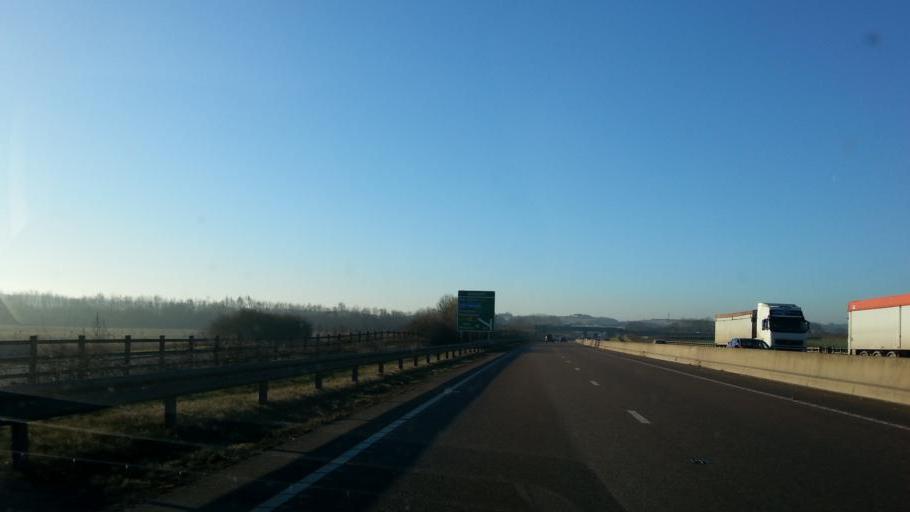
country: GB
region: England
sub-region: Nottinghamshire
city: Bingham
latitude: 52.9584
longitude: -0.9687
